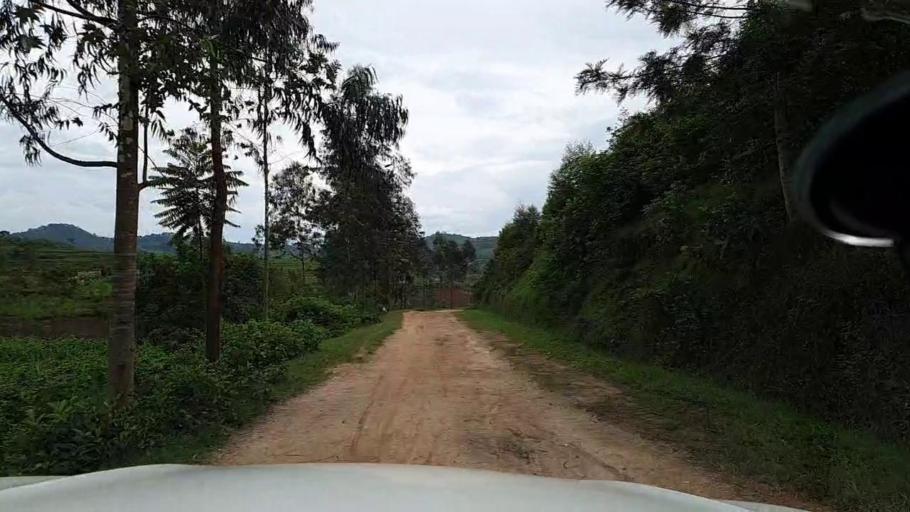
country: RW
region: Southern Province
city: Gitarama
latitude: -2.0918
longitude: 29.6408
